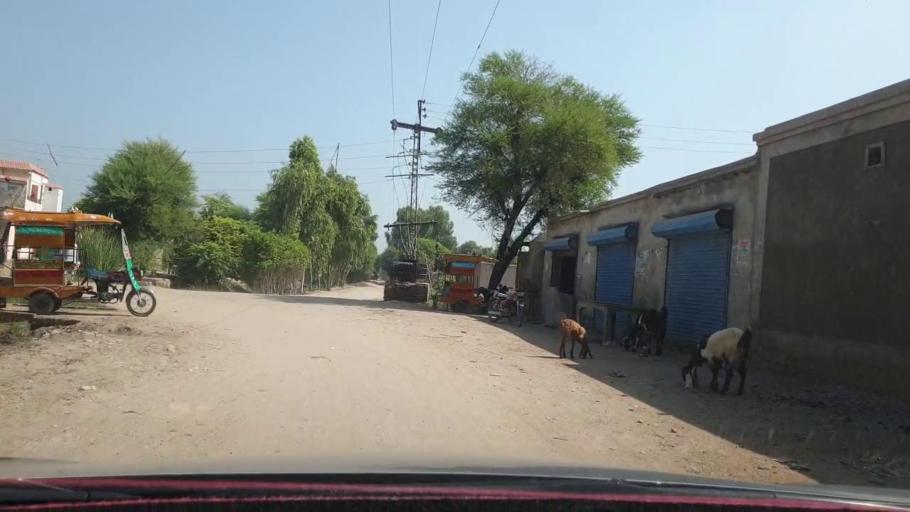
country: PK
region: Sindh
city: Warah
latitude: 27.4829
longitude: 67.8304
